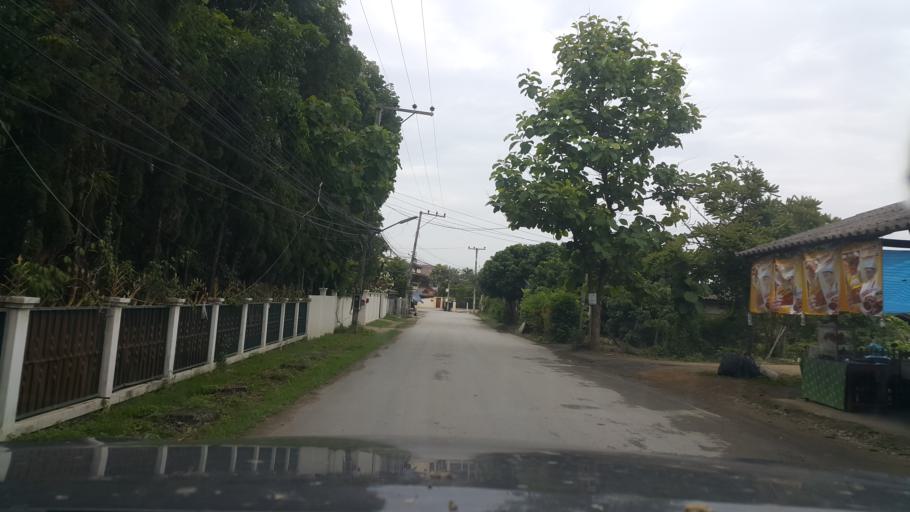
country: TH
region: Chiang Mai
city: San Pa Tong
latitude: 18.6679
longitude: 98.8340
